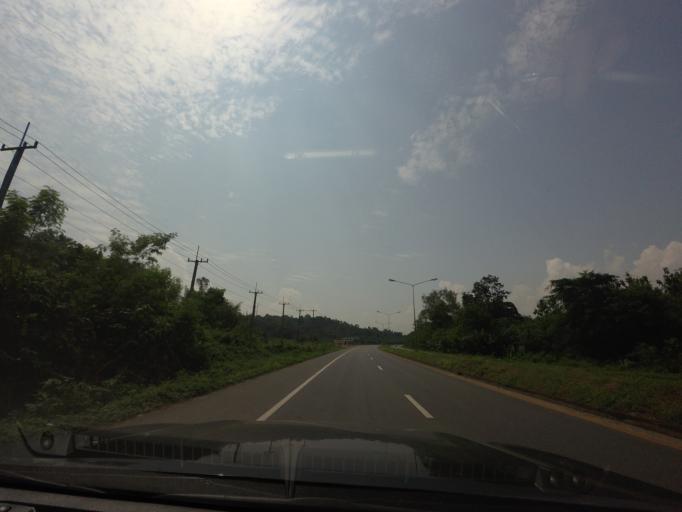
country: TH
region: Phrae
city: Den Chai
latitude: 17.9504
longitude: 100.0681
